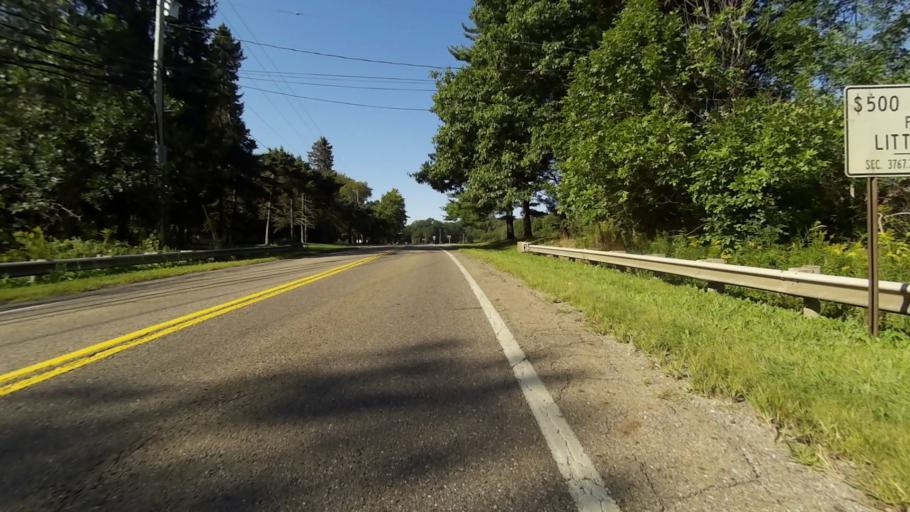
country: US
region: Ohio
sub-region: Portage County
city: Streetsboro
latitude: 41.2410
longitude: -81.3011
